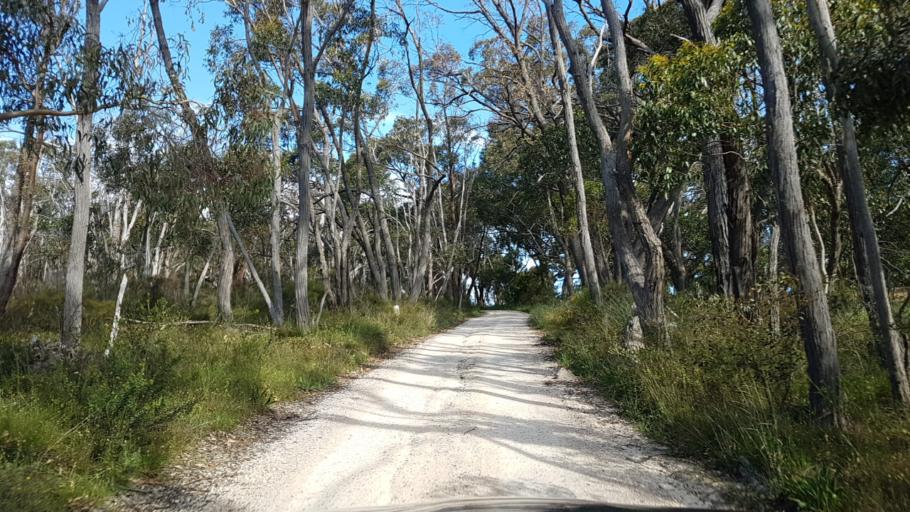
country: AU
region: South Australia
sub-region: Adelaide Hills
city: Adelaide Hills
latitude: -34.9061
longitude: 138.7364
